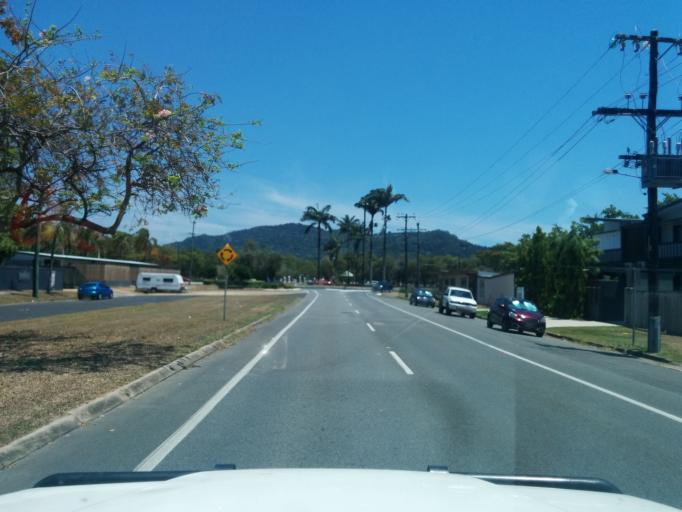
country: AU
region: Queensland
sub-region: Cairns
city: Cairns
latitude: -16.9138
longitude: 145.7554
